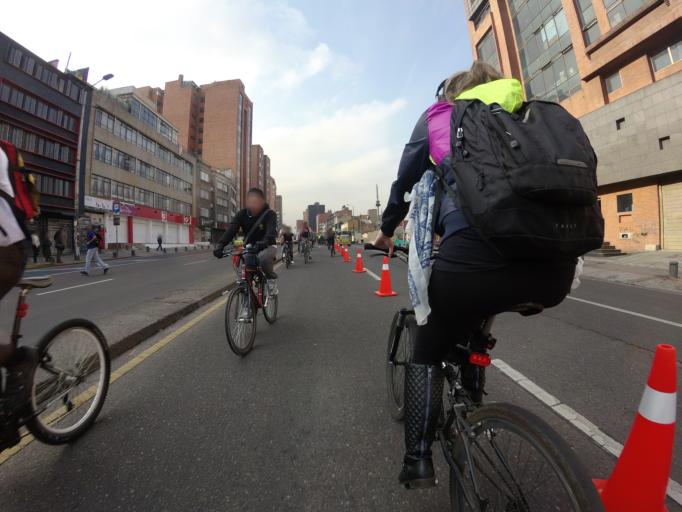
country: CO
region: Bogota D.C.
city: Bogota
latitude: 4.6371
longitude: -74.0635
